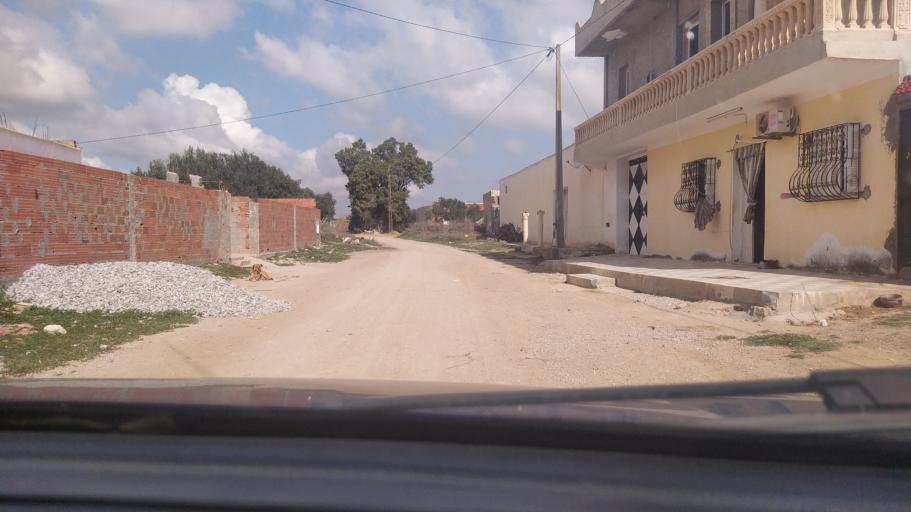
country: TN
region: Al Munastir
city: Sidi Bin Nur
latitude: 35.5289
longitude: 10.9548
